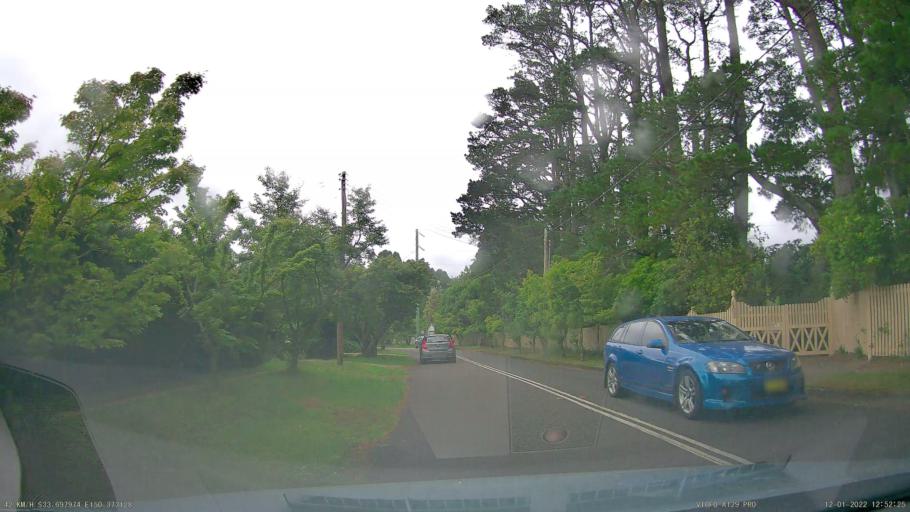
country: AU
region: New South Wales
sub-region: Blue Mountains Municipality
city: Leura
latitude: -33.6978
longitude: 150.3731
